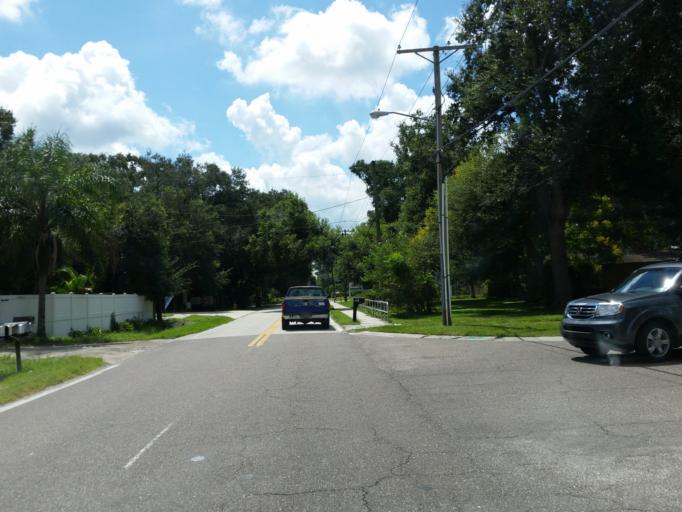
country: US
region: Florida
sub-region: Hillsborough County
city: Riverview
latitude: 27.8853
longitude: -82.3309
